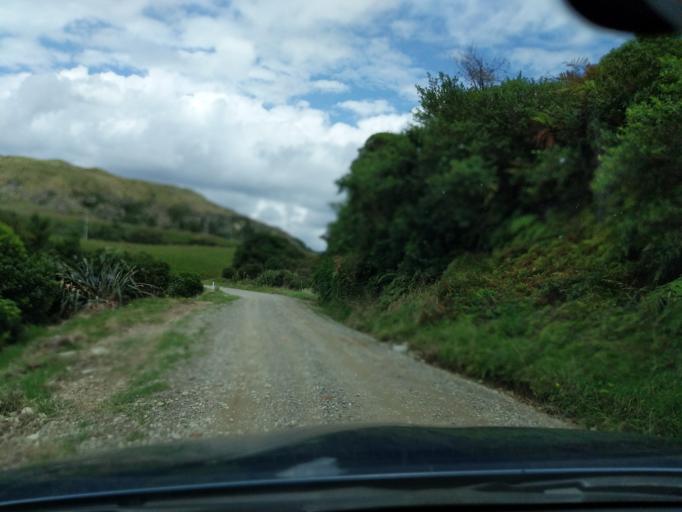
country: NZ
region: Tasman
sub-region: Tasman District
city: Takaka
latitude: -40.6683
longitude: 172.3990
